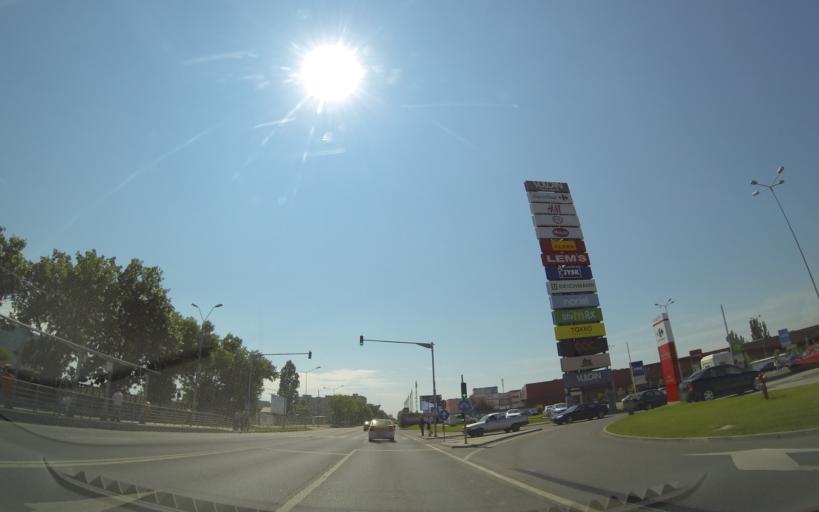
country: RO
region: Bucuresti
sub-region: Municipiul Bucuresti
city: Bucuresti
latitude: 44.4188
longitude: 26.0743
